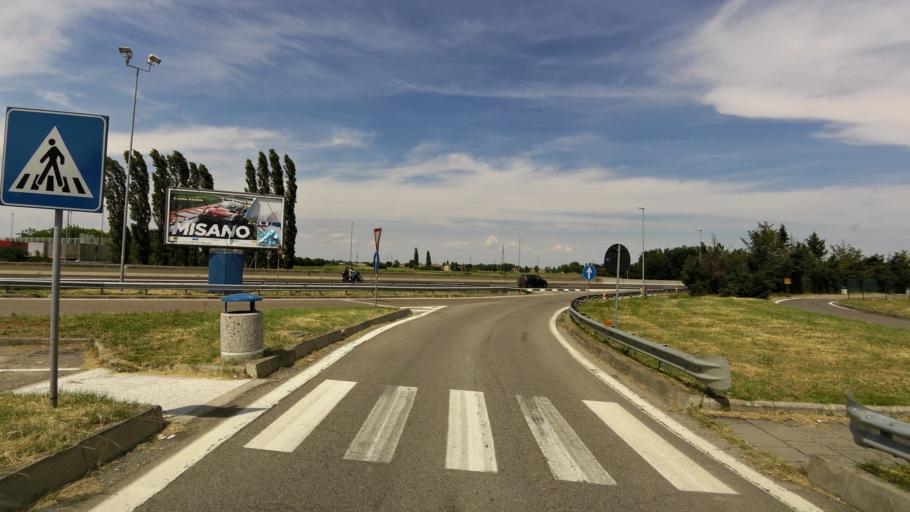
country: IT
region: Emilia-Romagna
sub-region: Provincia di Bologna
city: Anzola dell'Emilia
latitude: 44.5188
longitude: 11.2168
